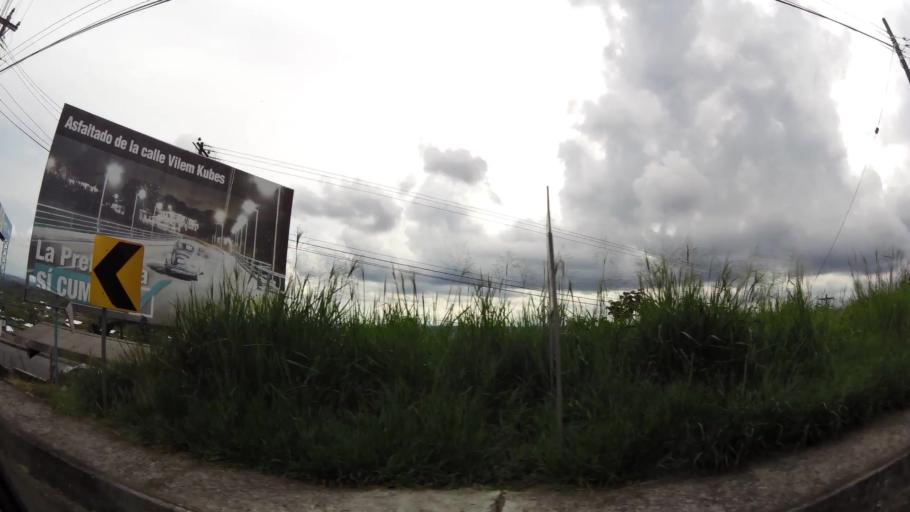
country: EC
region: Pastaza
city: Puyo
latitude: -1.5092
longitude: -78.0553
